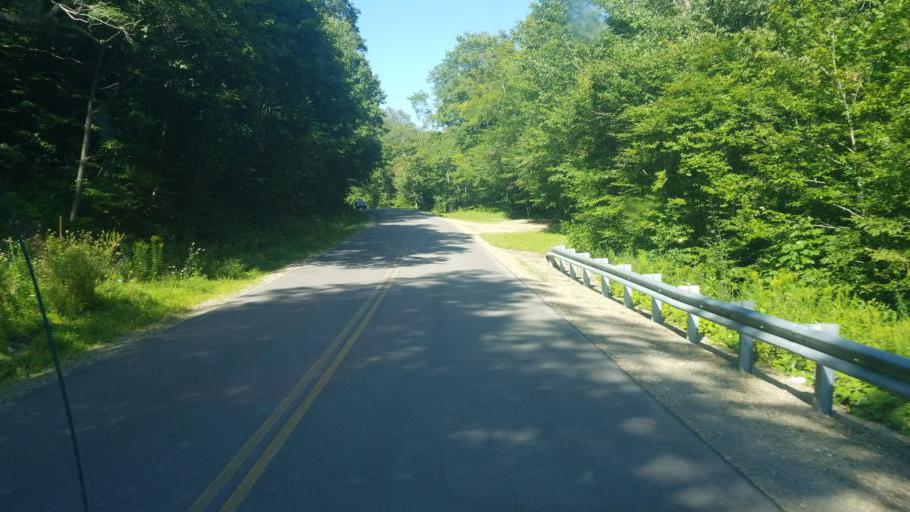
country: US
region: New York
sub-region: Allegany County
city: Wellsville
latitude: 42.0168
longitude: -77.9879
